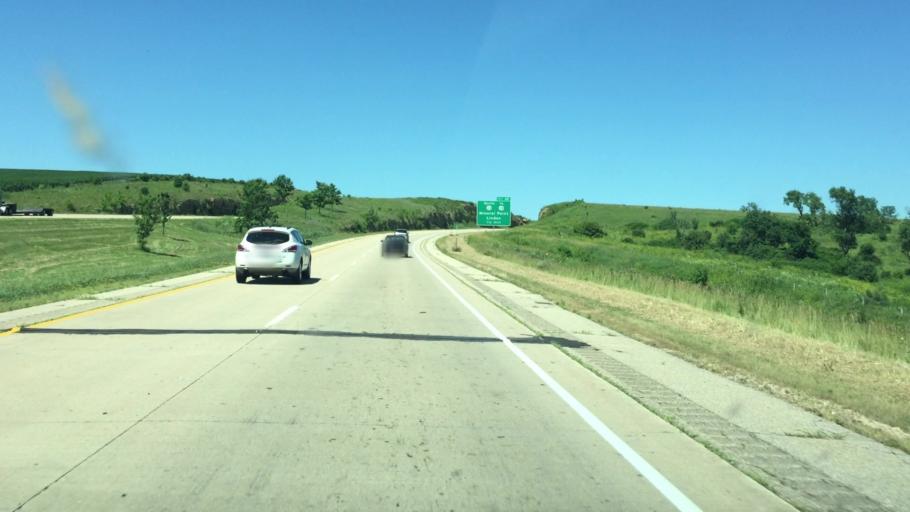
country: US
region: Wisconsin
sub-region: Iowa County
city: Mineral Point
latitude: 42.8727
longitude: -90.1923
